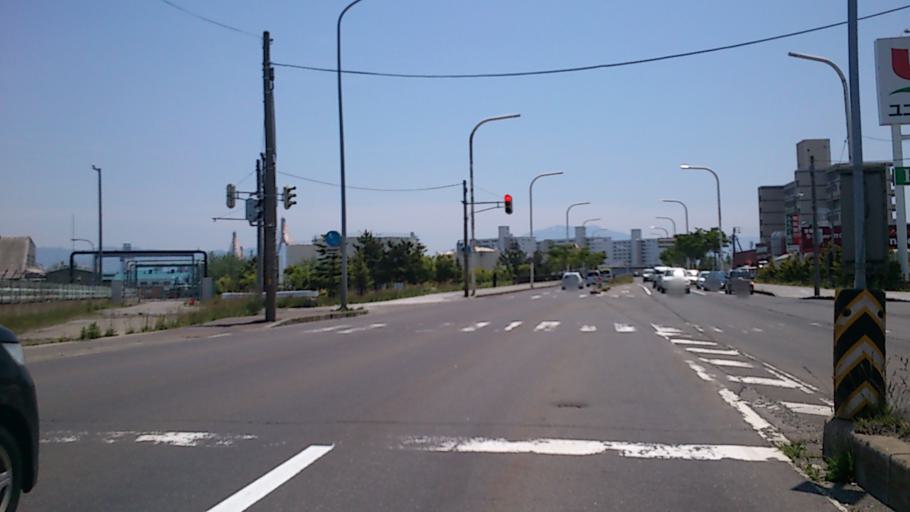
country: JP
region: Aomori
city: Aomori Shi
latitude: 40.8359
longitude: 140.7261
